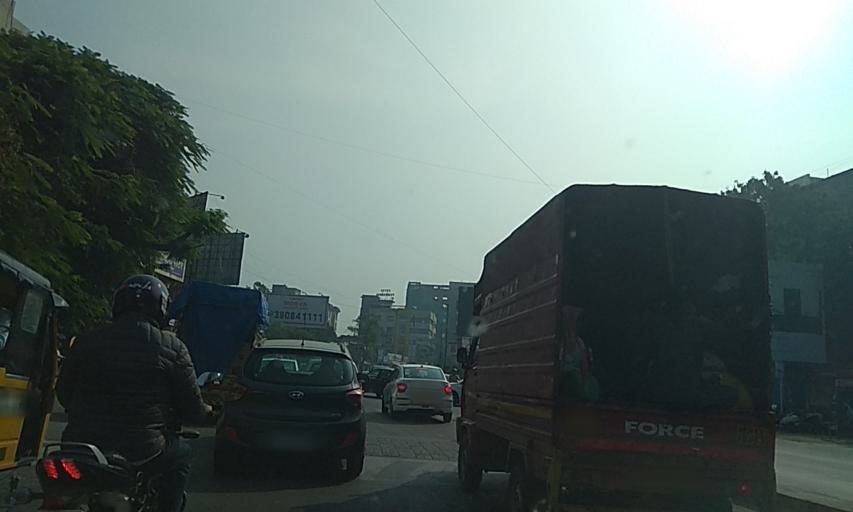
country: IN
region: Maharashtra
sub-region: Pune Division
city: Pimpri
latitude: 18.5616
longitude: 73.7861
